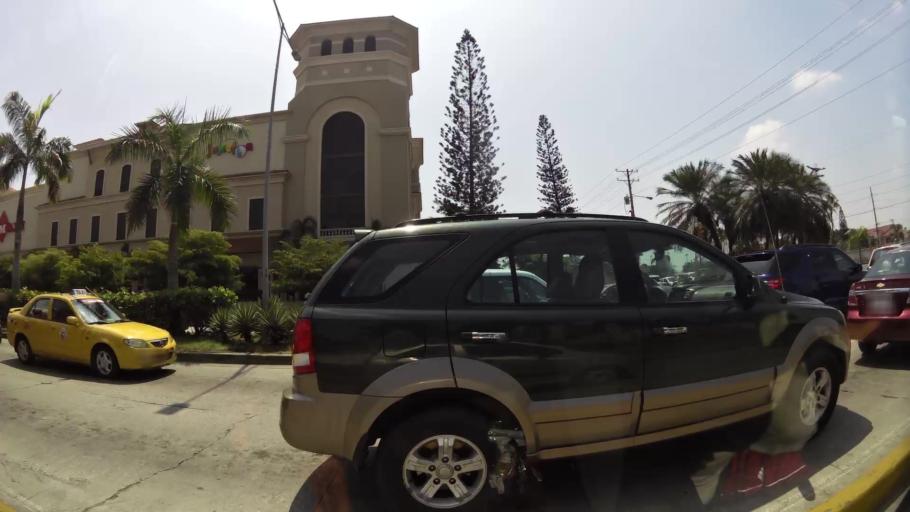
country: EC
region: Guayas
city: Eloy Alfaro
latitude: -2.1412
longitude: -79.8639
